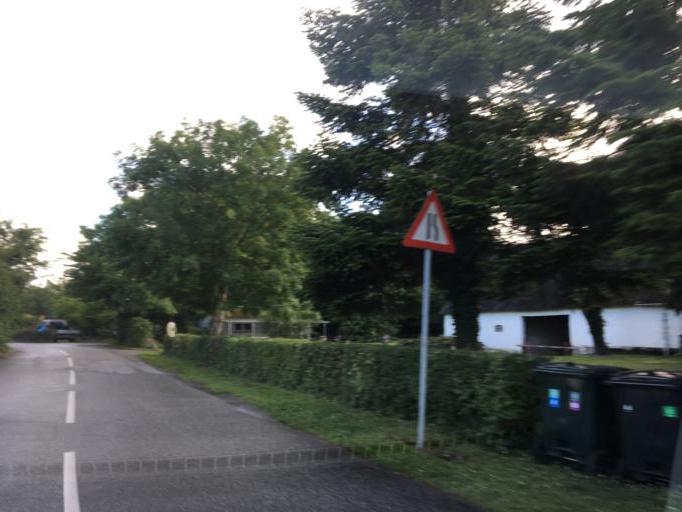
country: DK
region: Zealand
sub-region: Koge Kommune
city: Ejby
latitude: 55.5178
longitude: 12.0762
